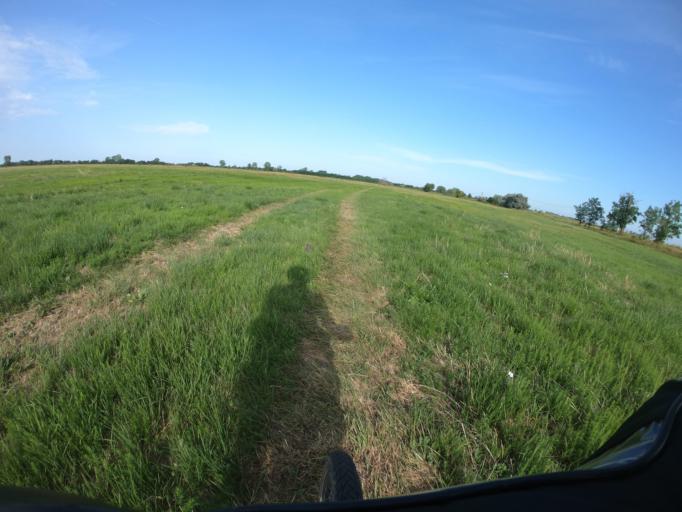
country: HU
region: Hajdu-Bihar
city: Tiszacsege
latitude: 47.6136
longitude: 21.0233
